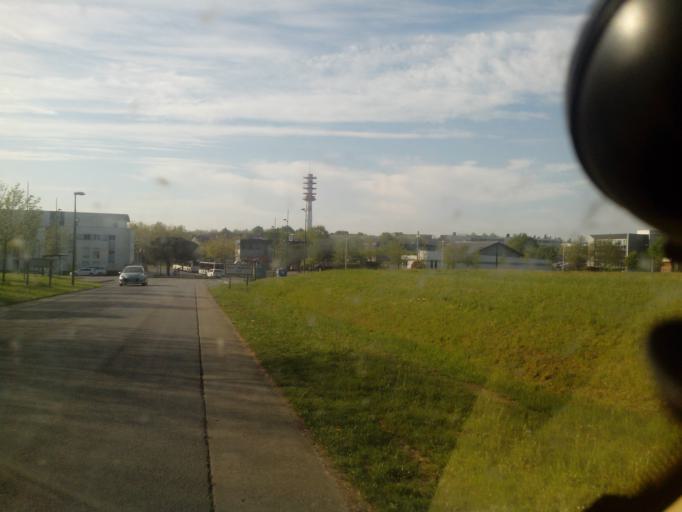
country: FR
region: Pays de la Loire
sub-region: Departement de la Loire-Atlantique
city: Saint-Herblain
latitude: 47.2312
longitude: -1.6176
